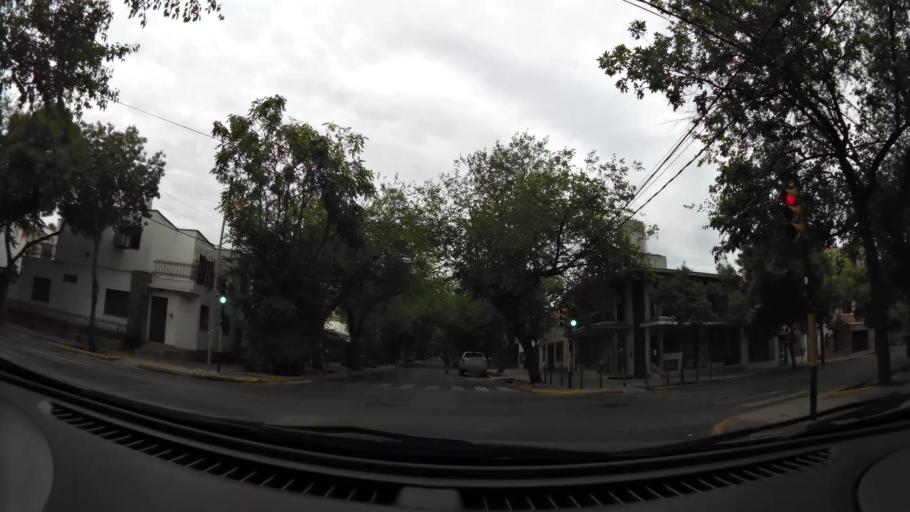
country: AR
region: Mendoza
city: Mendoza
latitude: -32.9011
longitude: -68.8492
